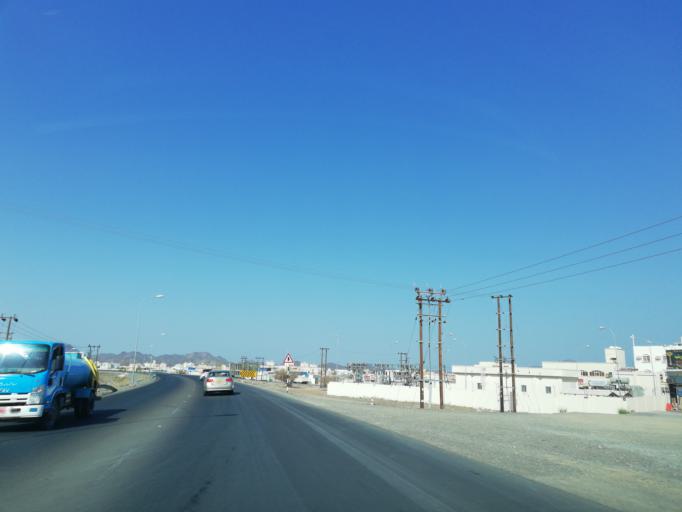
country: OM
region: Ash Sharqiyah
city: Ibra'
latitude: 22.7937
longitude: 58.1506
